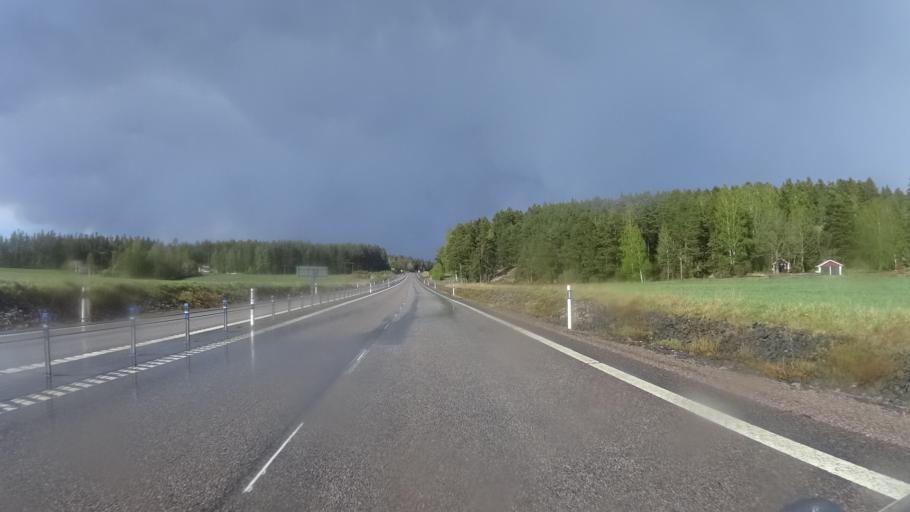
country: SE
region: OErebro
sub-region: Askersunds Kommun
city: Askersund
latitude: 58.7871
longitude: 14.8133
